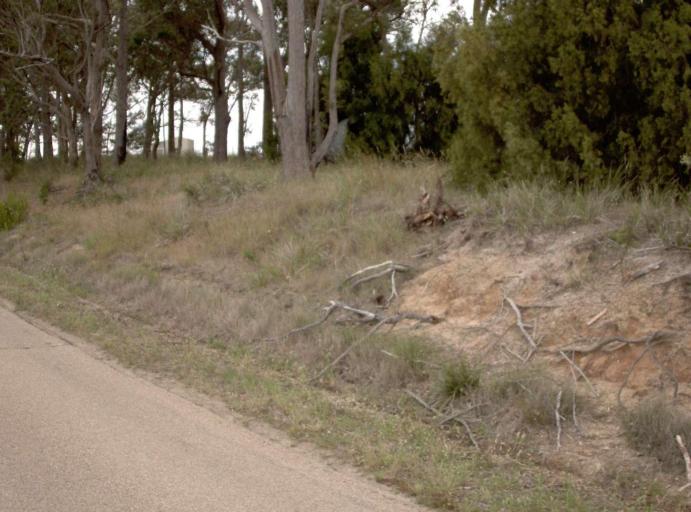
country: AU
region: Victoria
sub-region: East Gippsland
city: Bairnsdale
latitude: -37.7376
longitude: 147.5955
